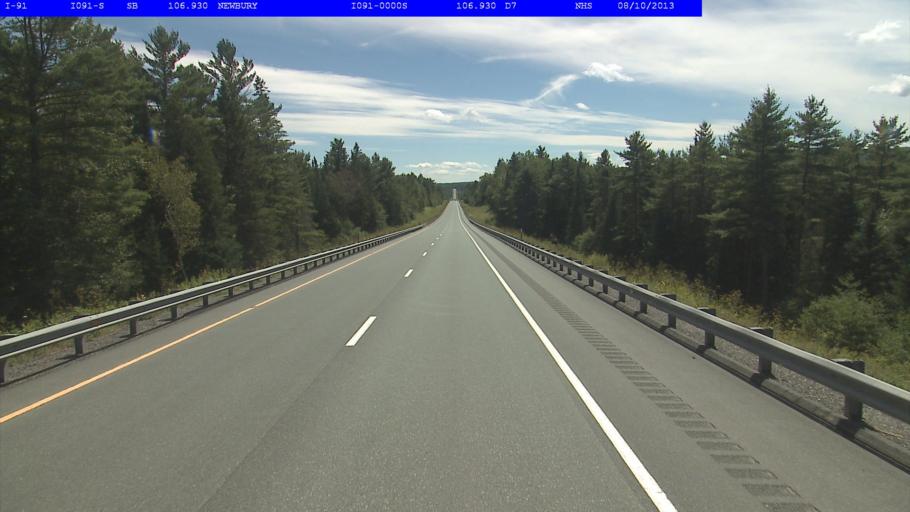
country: US
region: New Hampshire
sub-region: Grafton County
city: Woodsville
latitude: 44.1136
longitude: -72.1071
